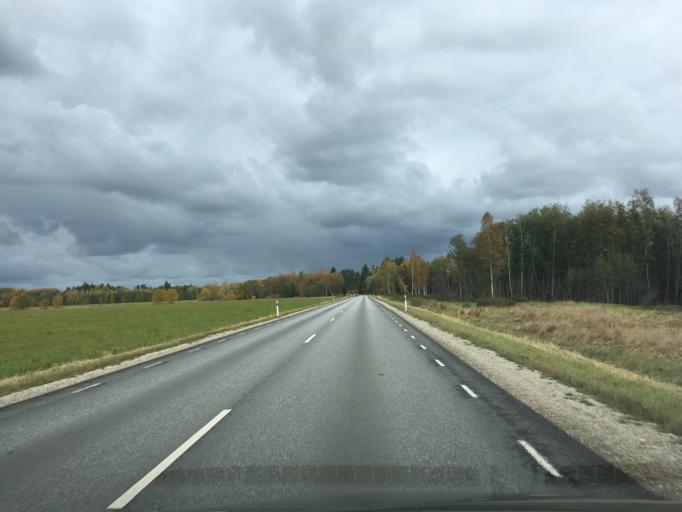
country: EE
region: Harju
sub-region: Anija vald
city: Kehra
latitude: 59.2873
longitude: 25.3750
